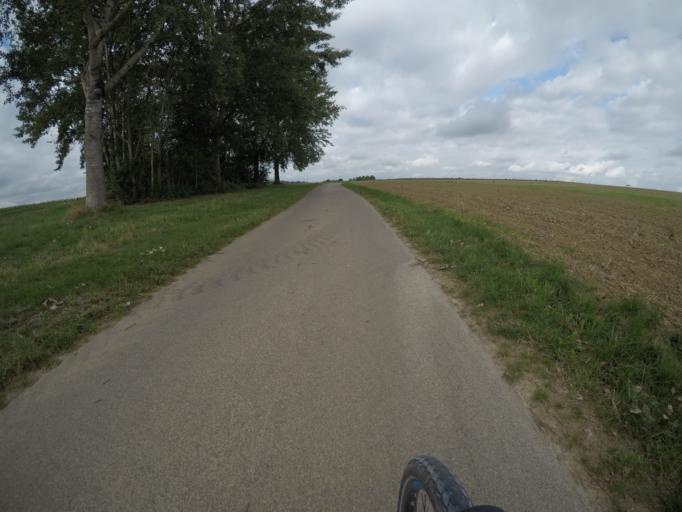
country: DE
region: Baden-Wuerttemberg
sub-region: Regierungsbezirk Stuttgart
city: Renningen
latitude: 48.7377
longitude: 8.9281
